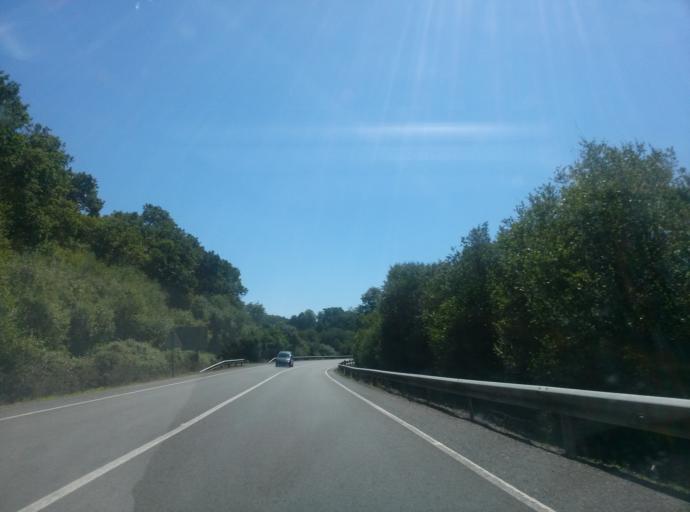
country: ES
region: Galicia
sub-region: Provincia de Lugo
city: Castro de Rei
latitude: 43.1139
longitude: -7.4499
